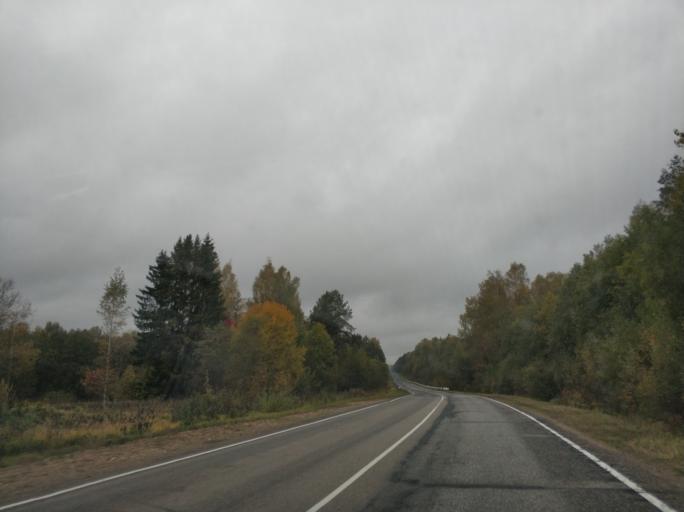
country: RU
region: Pskov
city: Sebezh
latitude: 56.2108
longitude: 28.6412
